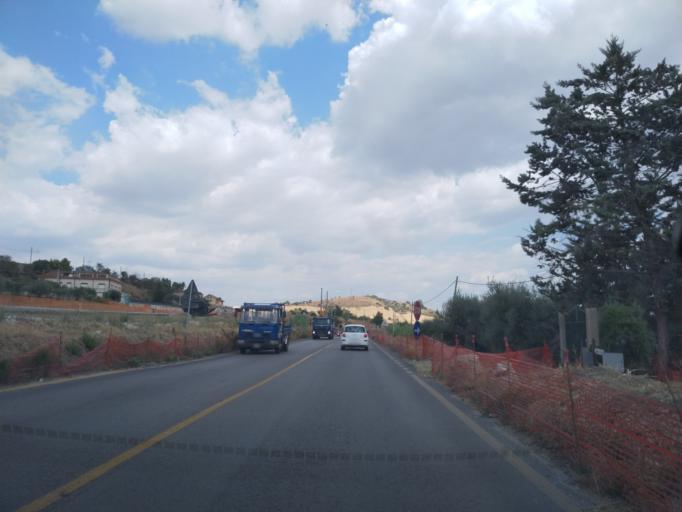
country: IT
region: Sicily
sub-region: Provincia di Caltanissetta
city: San Cataldo
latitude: 37.4545
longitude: 13.9858
